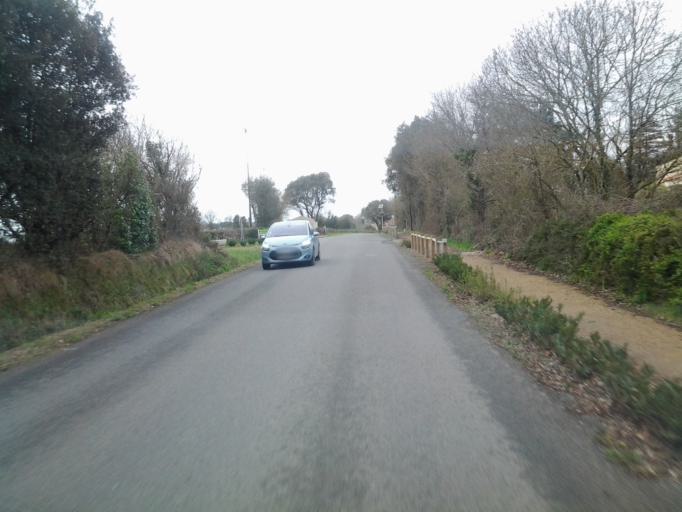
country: FR
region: Pays de la Loire
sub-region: Departement de la Vendee
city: Avrille
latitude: 46.4629
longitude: -1.4877
